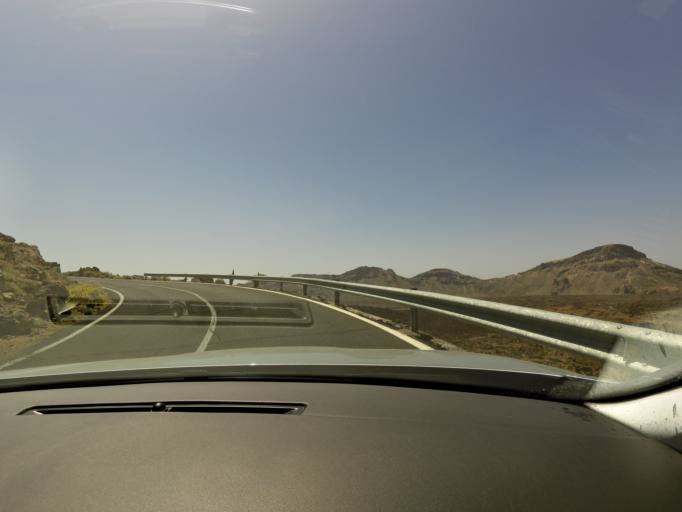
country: ES
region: Canary Islands
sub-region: Provincia de Santa Cruz de Tenerife
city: Vilaflor
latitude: 28.2580
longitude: -16.6126
